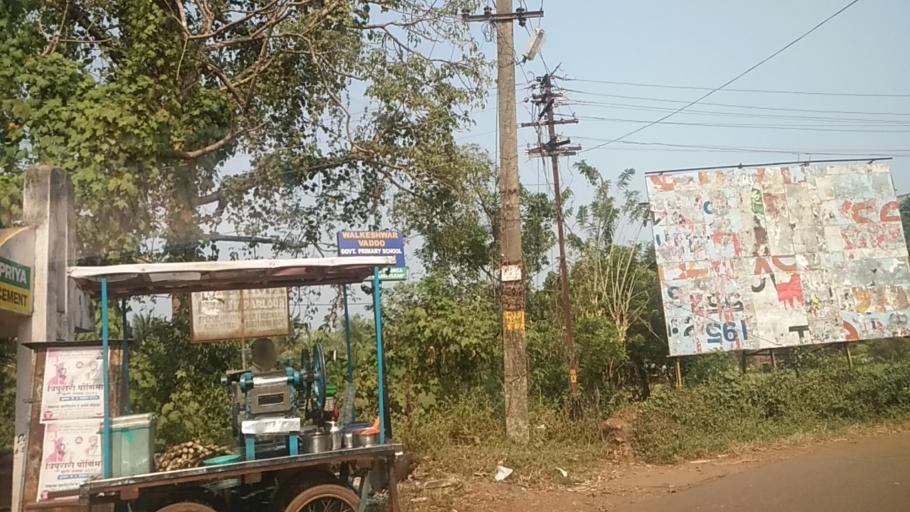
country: IN
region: Goa
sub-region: North Goa
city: Panaji
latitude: 15.5079
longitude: 73.8310
